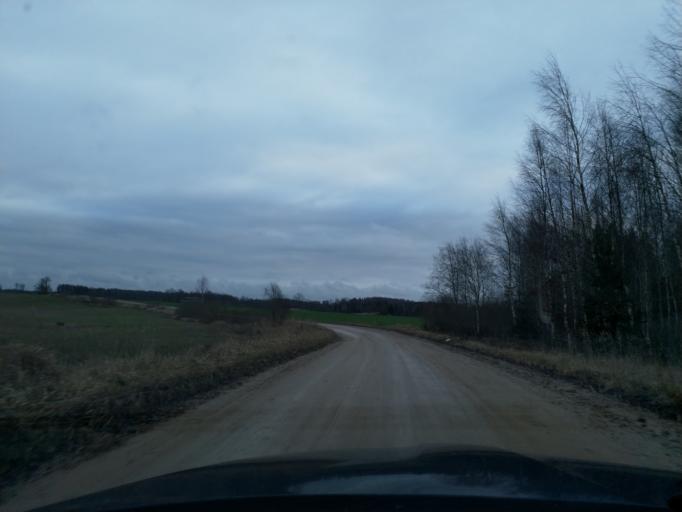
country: LV
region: Saldus Rajons
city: Saldus
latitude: 56.8928
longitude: 22.2693
